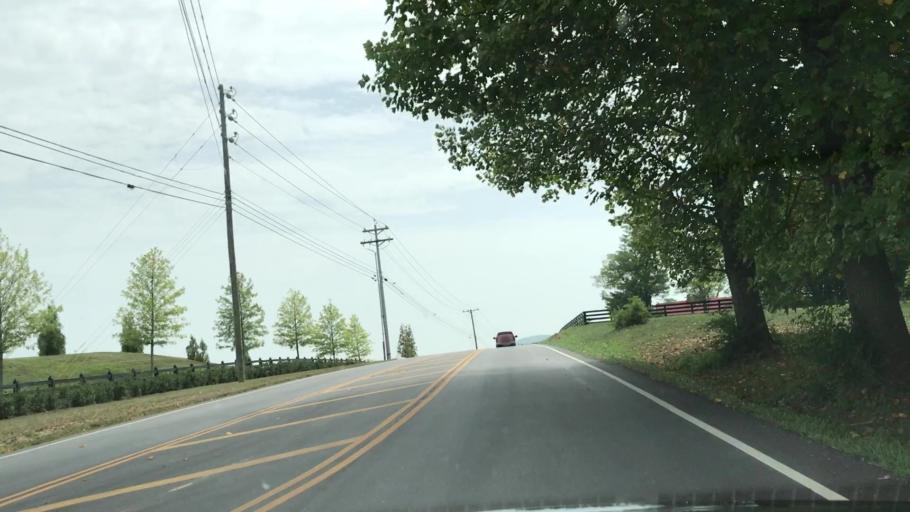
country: US
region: Tennessee
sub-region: Williamson County
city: Nolensville
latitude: 35.9378
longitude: -86.7049
